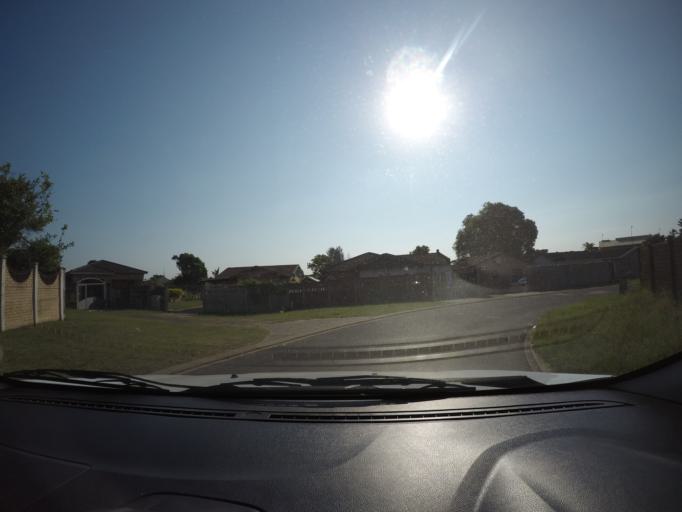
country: ZA
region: KwaZulu-Natal
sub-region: uThungulu District Municipality
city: Richards Bay
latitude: -28.7163
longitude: 32.0373
